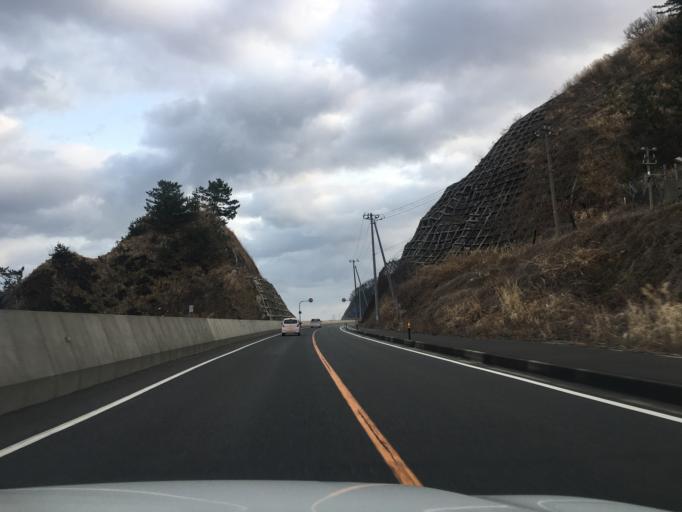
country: JP
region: Yamagata
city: Tsuruoka
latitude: 38.5855
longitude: 139.5604
